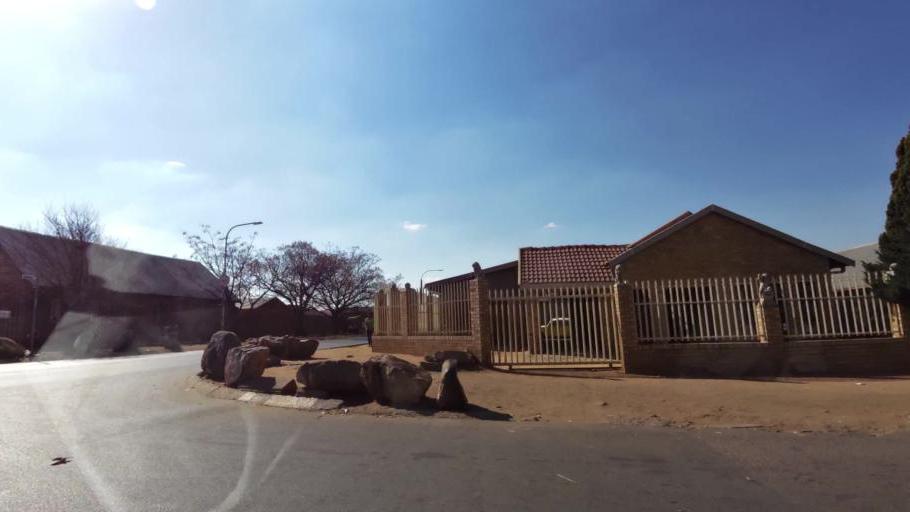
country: ZA
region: Gauteng
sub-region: City of Johannesburg Metropolitan Municipality
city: Soweto
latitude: -26.2332
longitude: 27.8808
